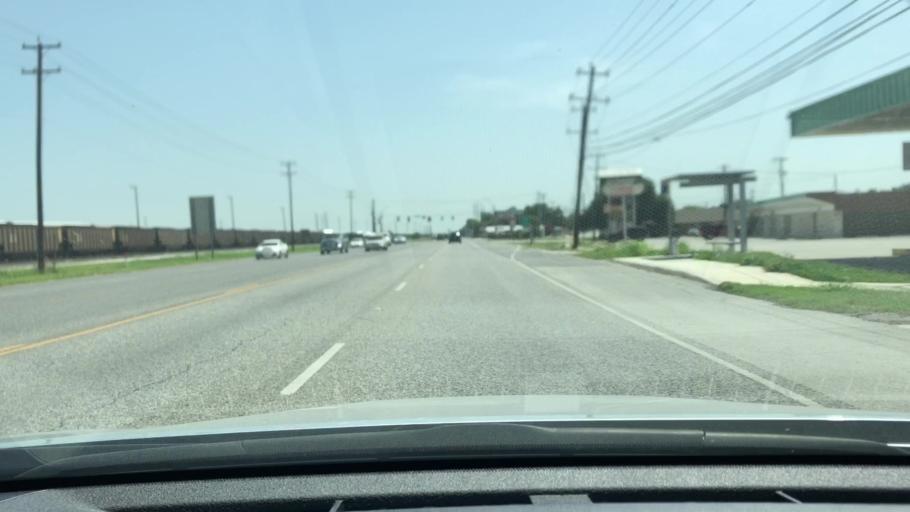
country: US
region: Texas
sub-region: Bexar County
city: Kirby
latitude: 29.4625
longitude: -98.3992
